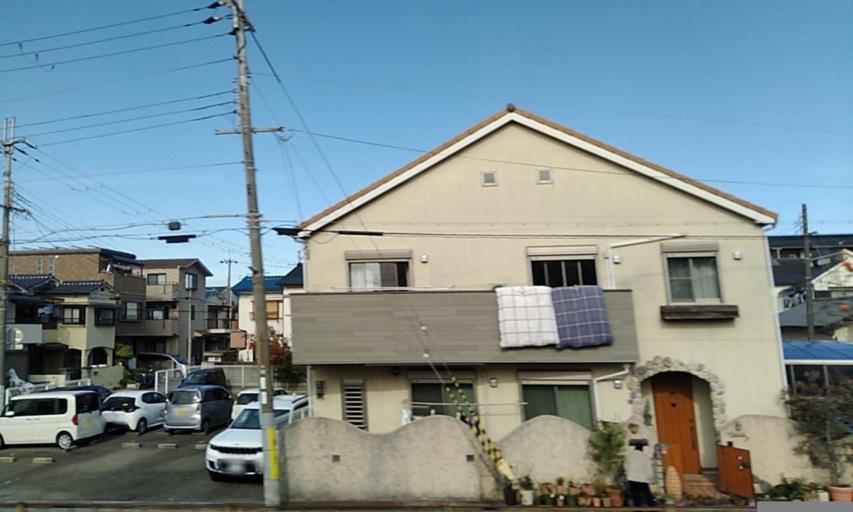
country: JP
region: Hyogo
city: Itami
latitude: 34.7500
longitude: 135.3824
